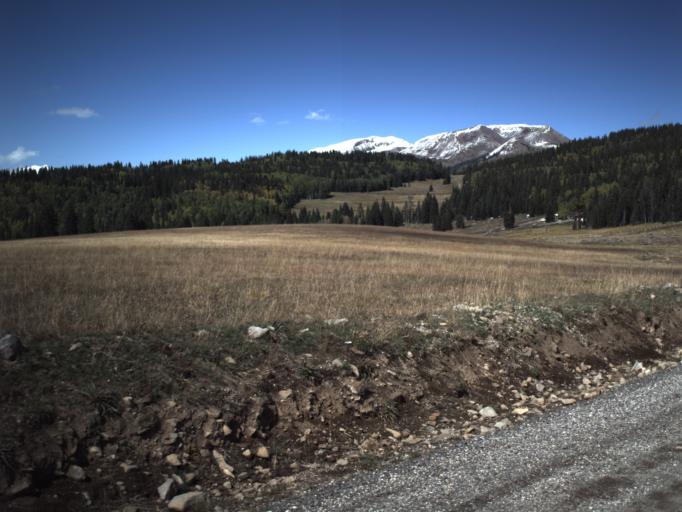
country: US
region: Utah
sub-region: Piute County
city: Junction
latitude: 38.2826
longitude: -112.3595
